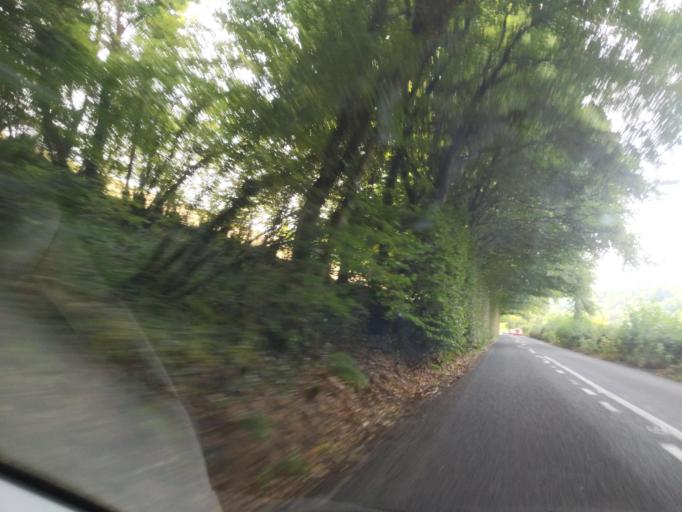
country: GB
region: England
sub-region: Devon
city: Winkleigh
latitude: 50.9556
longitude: -3.9283
